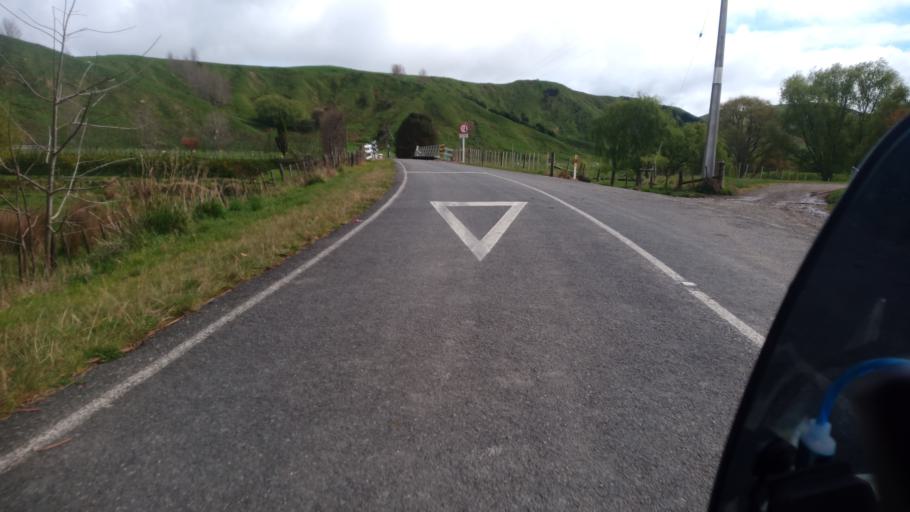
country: NZ
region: Gisborne
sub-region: Gisborne District
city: Gisborne
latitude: -38.5760
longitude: 178.1734
